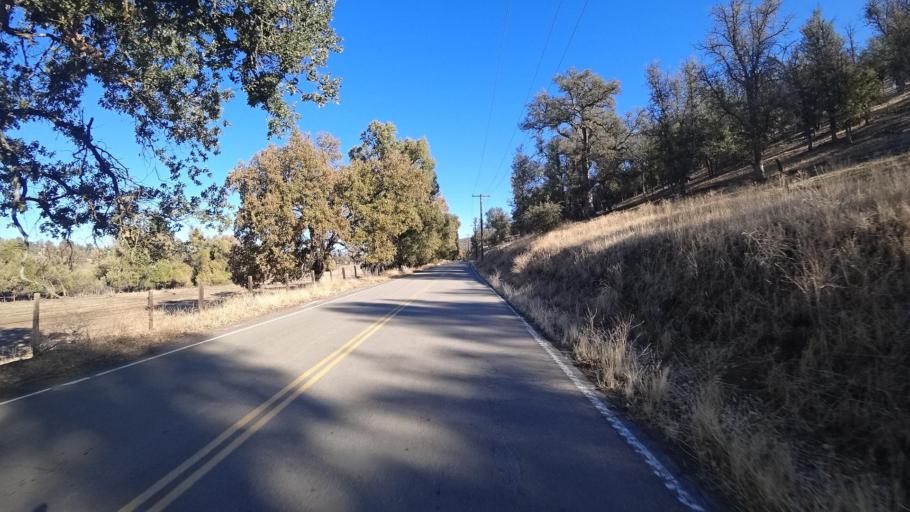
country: US
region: California
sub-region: Kern County
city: Alta Sierra
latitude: 35.7364
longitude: -118.7196
